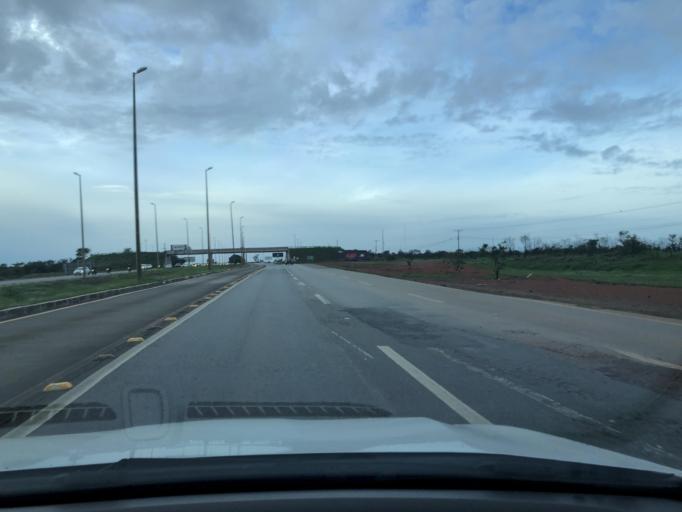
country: BR
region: Federal District
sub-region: Brasilia
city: Brasilia
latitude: -15.9705
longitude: -47.9911
